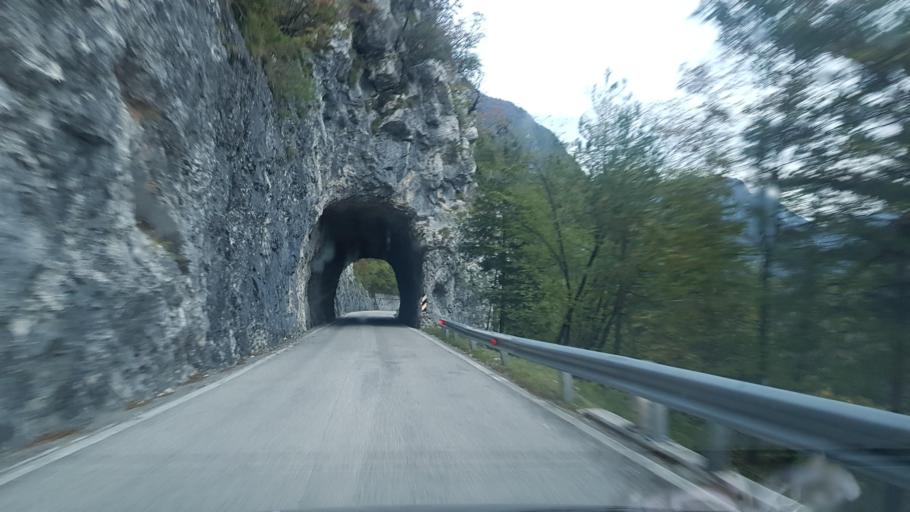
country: IT
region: Friuli Venezia Giulia
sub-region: Provincia di Udine
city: Villa Santina
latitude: 46.3476
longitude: 12.9173
